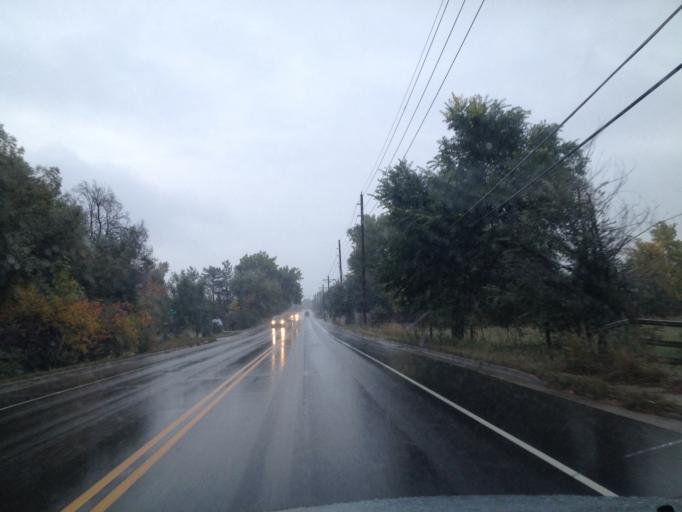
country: US
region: Colorado
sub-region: Boulder County
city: Superior
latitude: 39.9916
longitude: -105.1752
